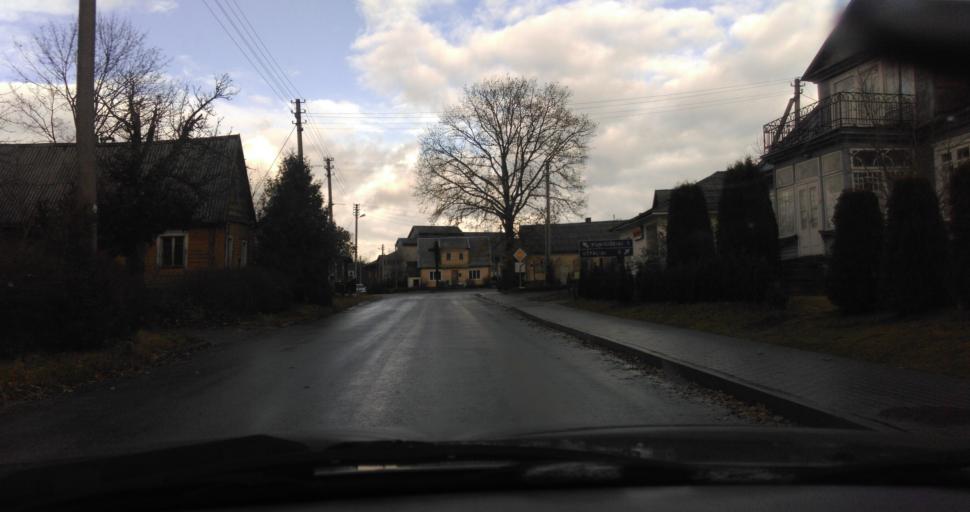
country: LT
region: Utenos apskritis
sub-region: Utena
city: Utena
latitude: 55.5862
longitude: 25.4965
